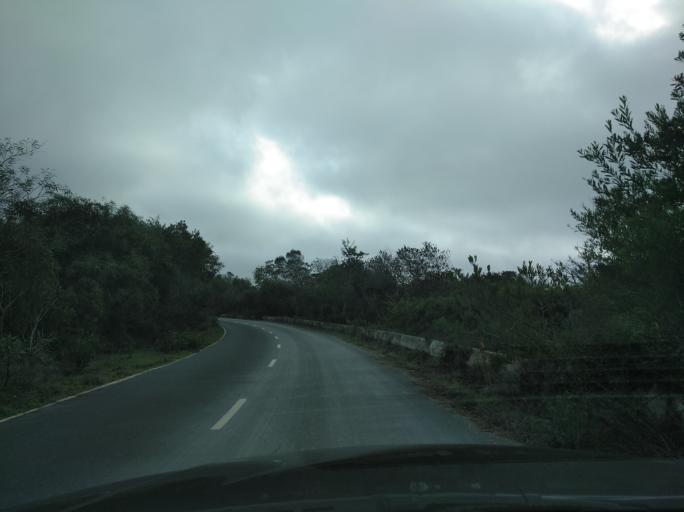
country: PT
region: Beja
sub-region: Odemira
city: Vila Nova de Milfontes
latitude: 37.7183
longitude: -8.7820
